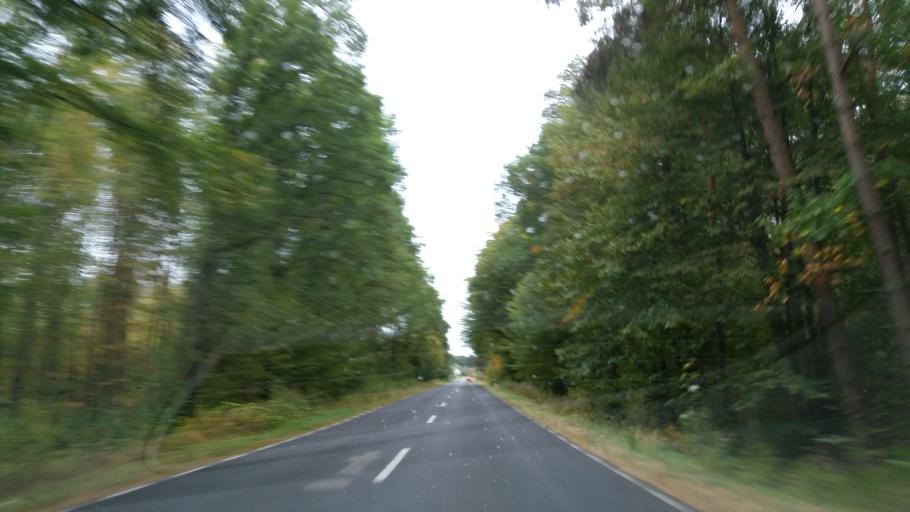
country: PL
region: Lubusz
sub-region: Powiat gorzowski
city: Klodawa
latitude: 52.8897
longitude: 15.1918
